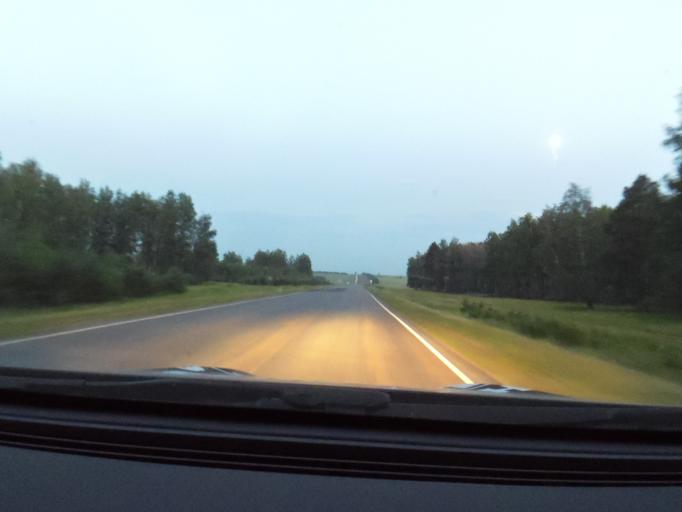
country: RU
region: Bashkortostan
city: Duvan
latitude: 56.0875
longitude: 58.0782
